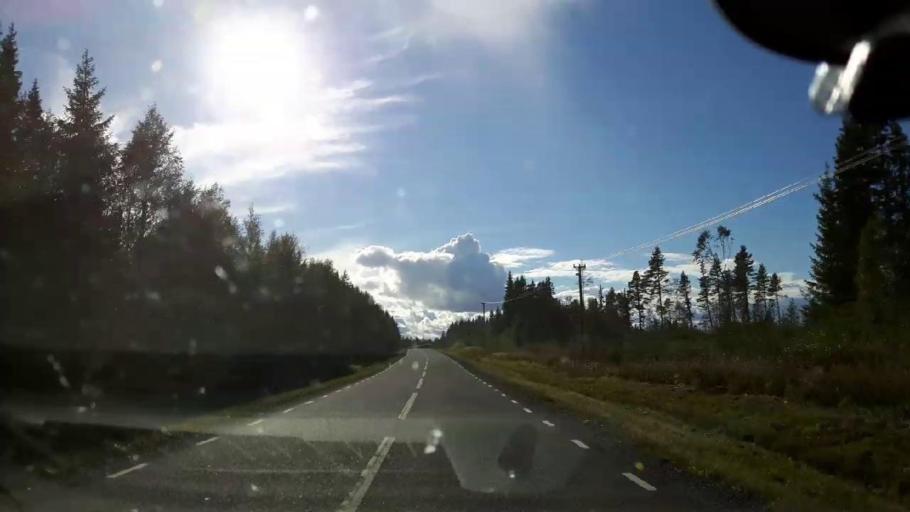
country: SE
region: Jaemtland
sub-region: Stroemsunds Kommun
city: Stroemsund
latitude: 63.5757
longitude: 15.6402
